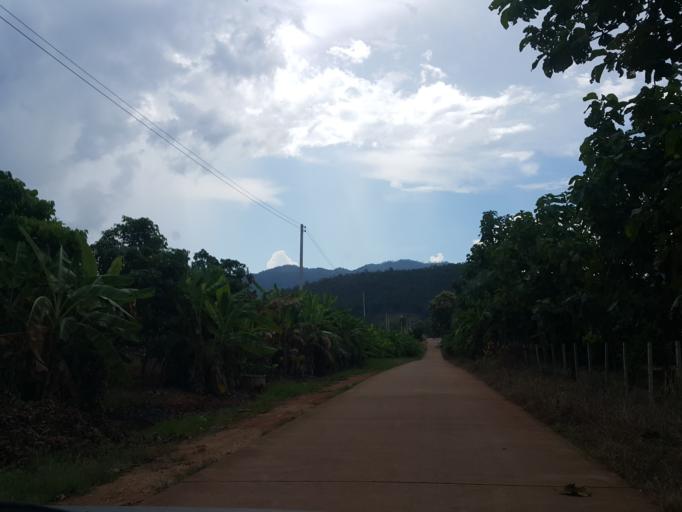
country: TH
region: Chiang Mai
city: Phrao
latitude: 19.3334
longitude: 99.1547
